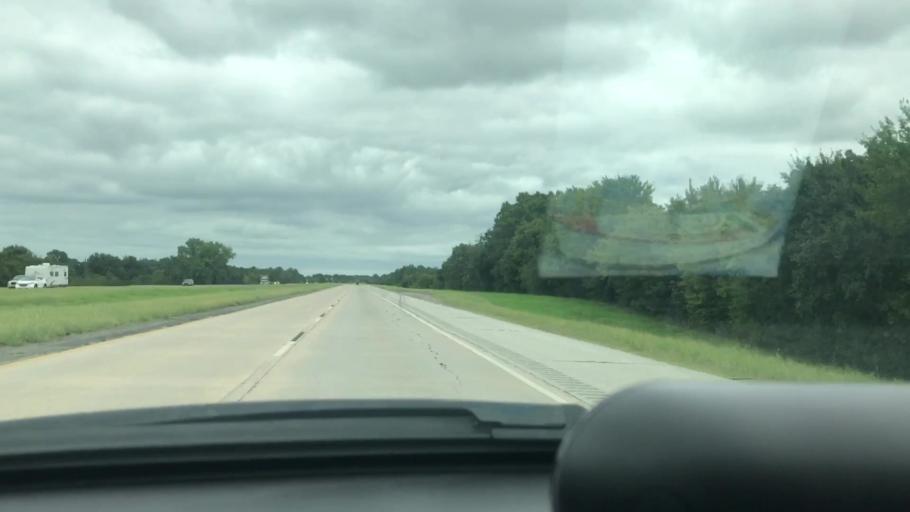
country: US
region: Oklahoma
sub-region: Wagoner County
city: Wagoner
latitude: 35.8966
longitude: -95.4024
